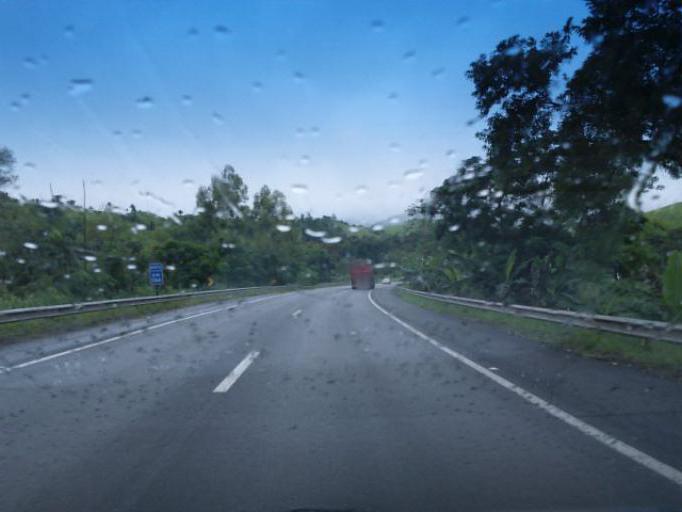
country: BR
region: Sao Paulo
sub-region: Cajati
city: Cajati
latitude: -24.7788
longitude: -48.1988
